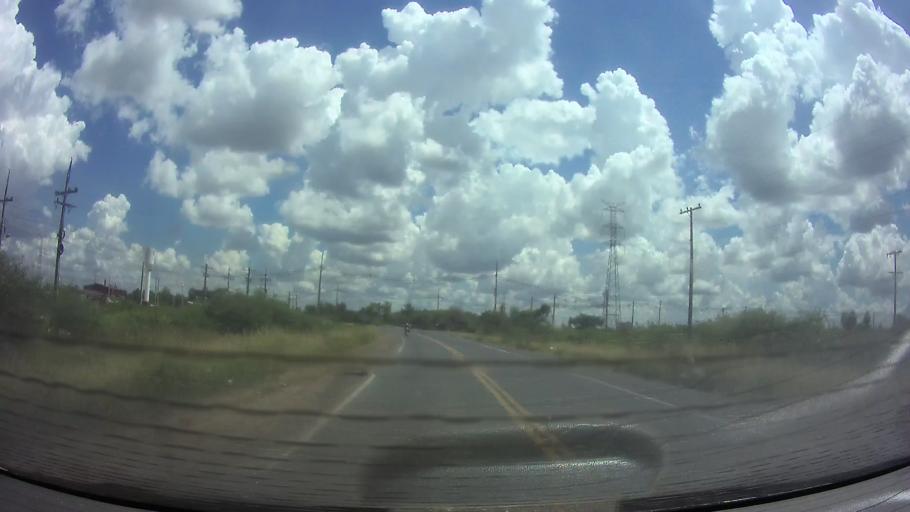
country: PY
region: Central
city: Colonia Mariano Roque Alonso
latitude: -25.1785
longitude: -57.5851
